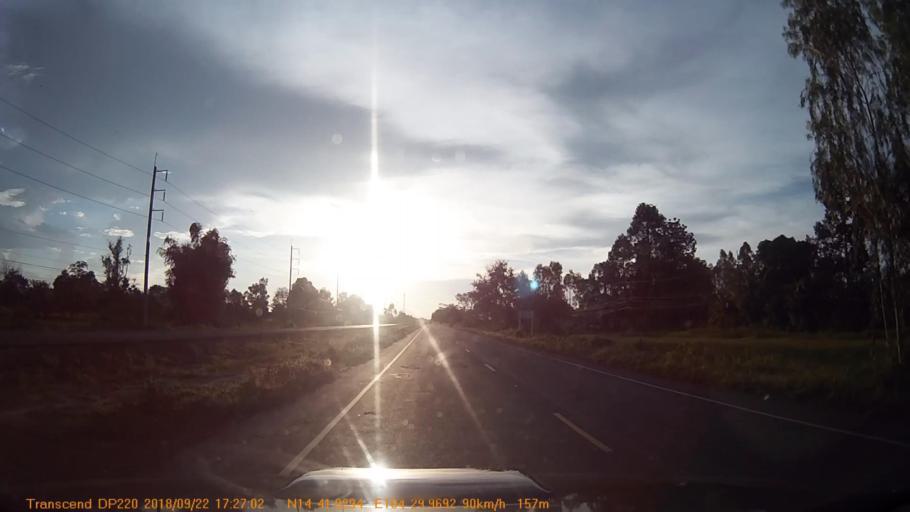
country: TH
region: Sisaket
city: Khun Han
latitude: 14.6839
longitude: 104.4991
